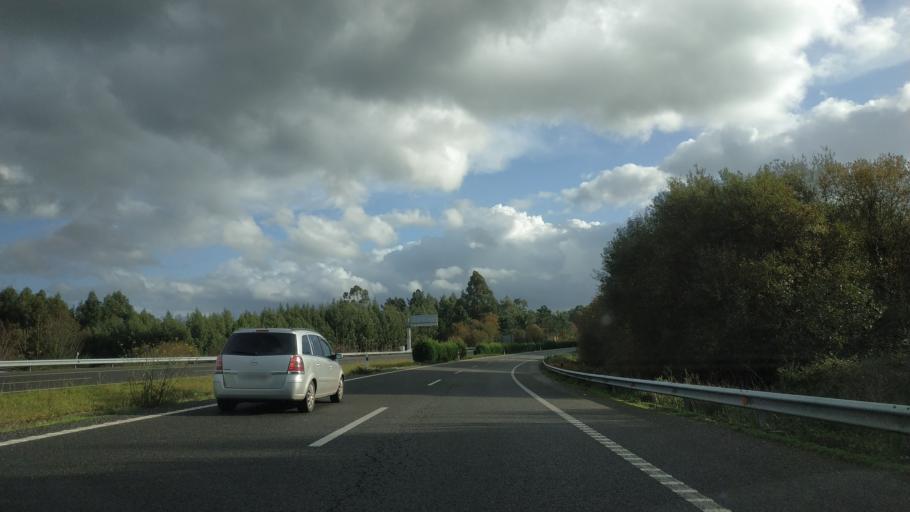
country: ES
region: Galicia
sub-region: Provincia da Coruna
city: Cambre
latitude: 43.2688
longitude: -8.3576
